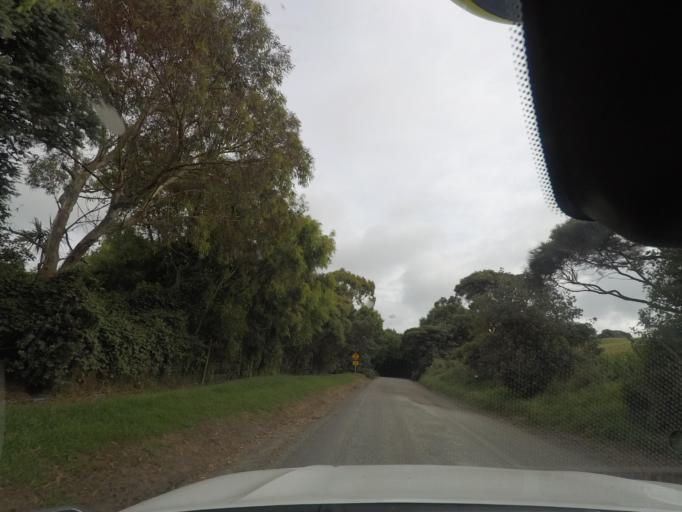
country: NZ
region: Auckland
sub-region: Auckland
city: Parakai
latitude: -36.4792
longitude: 174.2552
